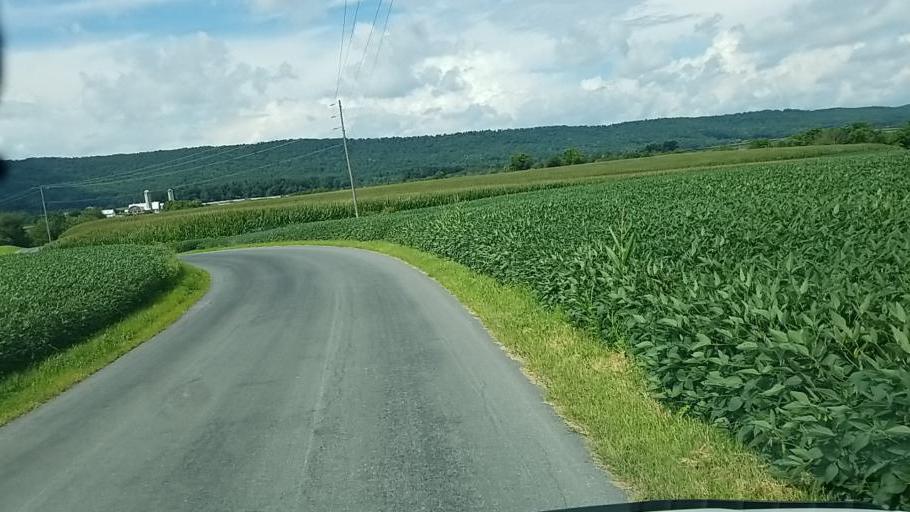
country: US
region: Pennsylvania
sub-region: Dauphin County
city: Elizabethville
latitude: 40.5952
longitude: -76.8468
